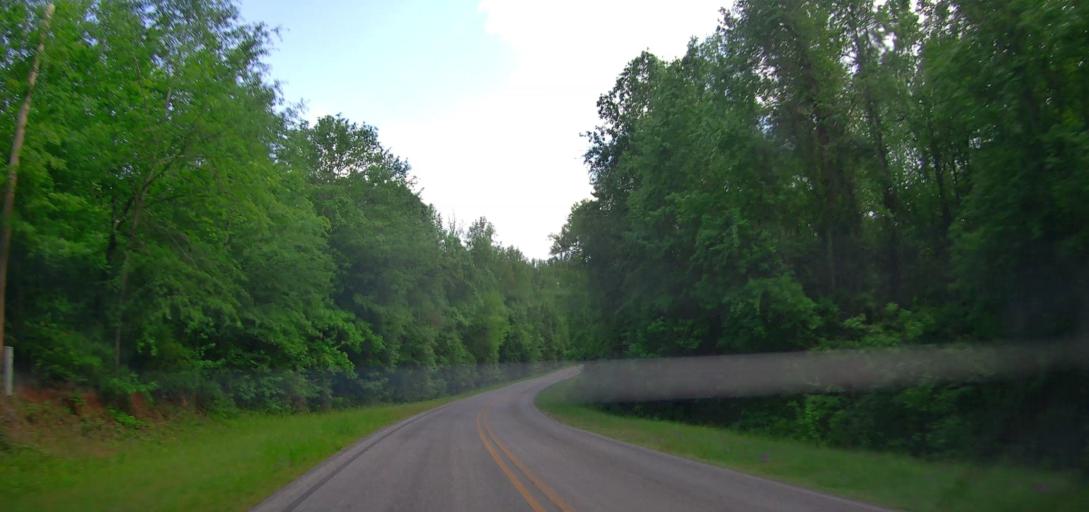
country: US
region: Georgia
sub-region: Laurens County
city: East Dublin
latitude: 32.6680
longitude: -82.8946
